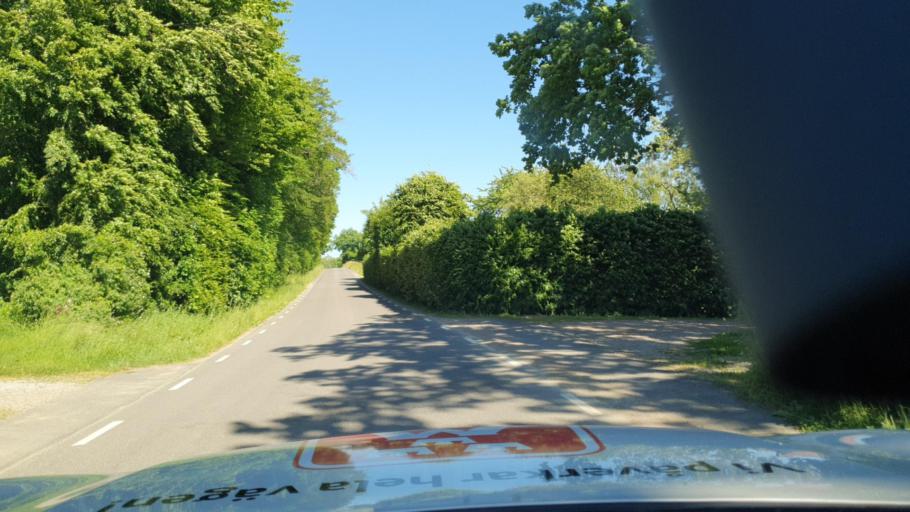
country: SE
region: Skane
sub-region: Sjobo Kommun
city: Sjoebo
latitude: 55.6506
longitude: 13.7487
